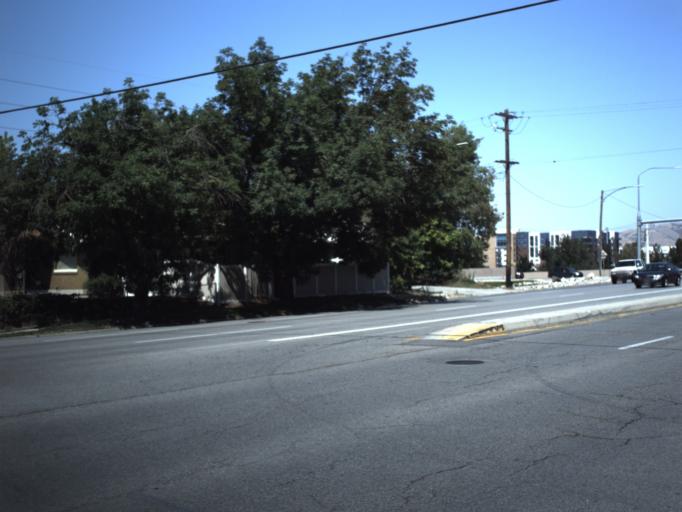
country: US
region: Utah
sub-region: Salt Lake County
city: Willard
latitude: 40.7182
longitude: -111.8535
